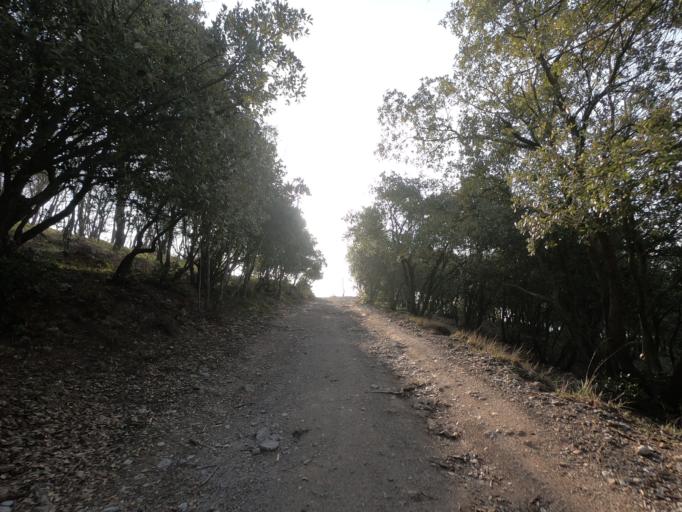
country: IT
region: Liguria
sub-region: Provincia di Savona
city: Balestrino
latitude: 44.1062
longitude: 8.1592
